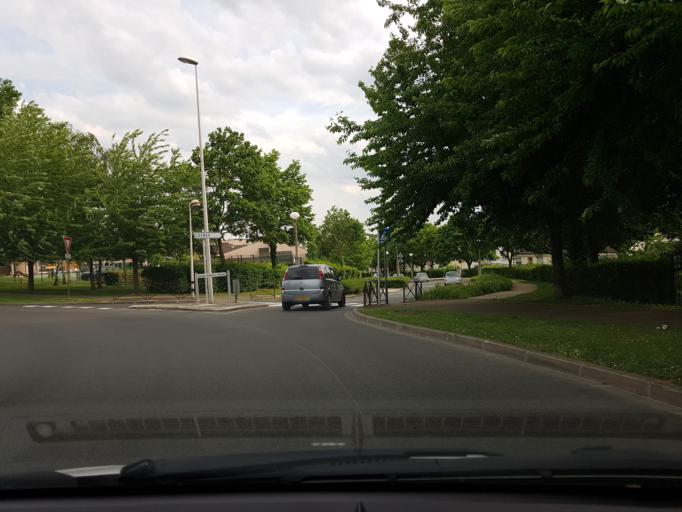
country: FR
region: Ile-de-France
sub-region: Departement de Seine-et-Marne
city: Torcy
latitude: 48.8427
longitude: 2.6514
